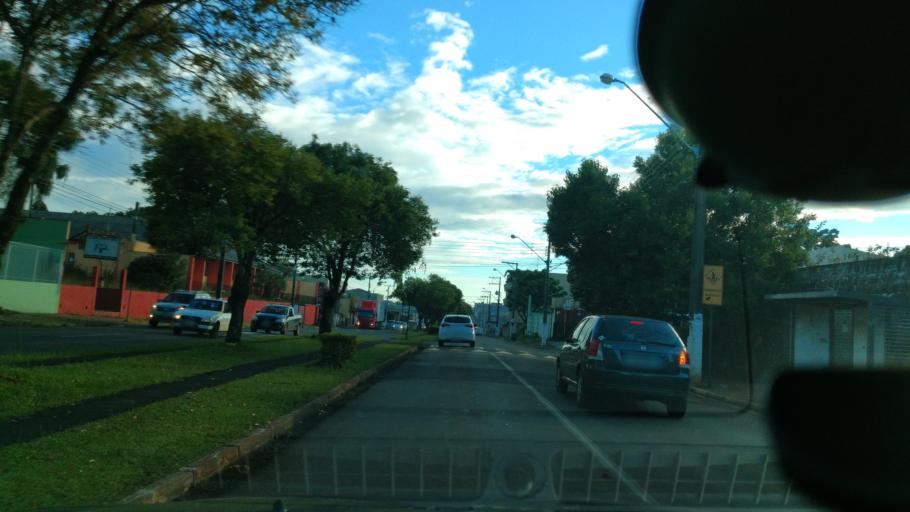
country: BR
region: Parana
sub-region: Guarapuava
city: Guarapuava
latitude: -25.3908
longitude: -51.4781
